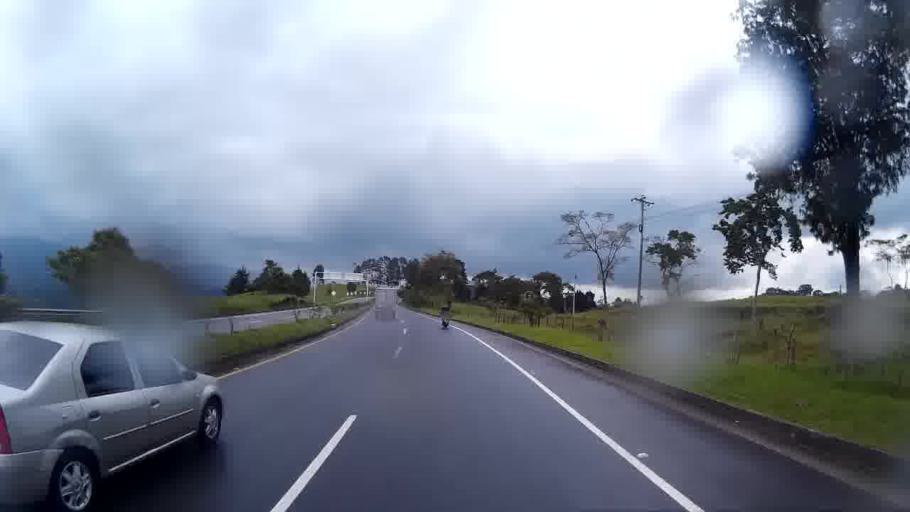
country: CO
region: Quindio
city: Salento
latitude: 4.6664
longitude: -75.5959
